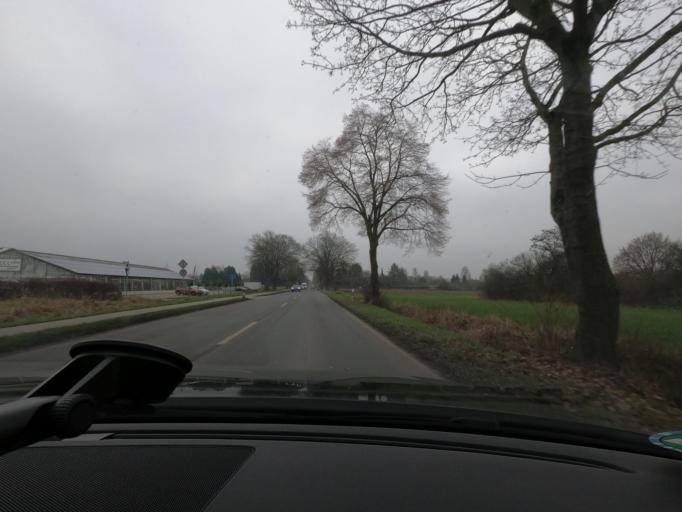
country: DE
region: North Rhine-Westphalia
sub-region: Regierungsbezirk Dusseldorf
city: Krefeld
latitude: 51.3728
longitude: 6.5637
